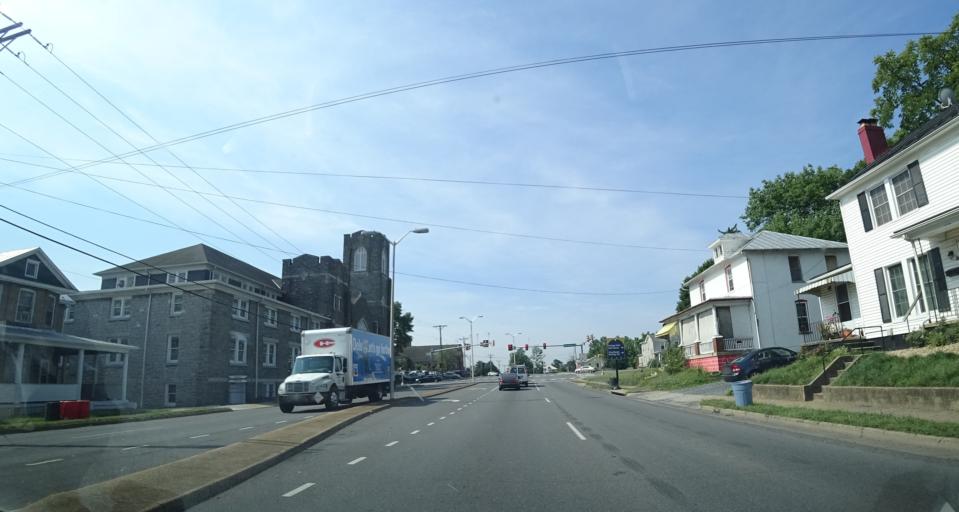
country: US
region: Virginia
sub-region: City of Harrisonburg
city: Harrisonburg
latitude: 38.4508
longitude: -78.8725
